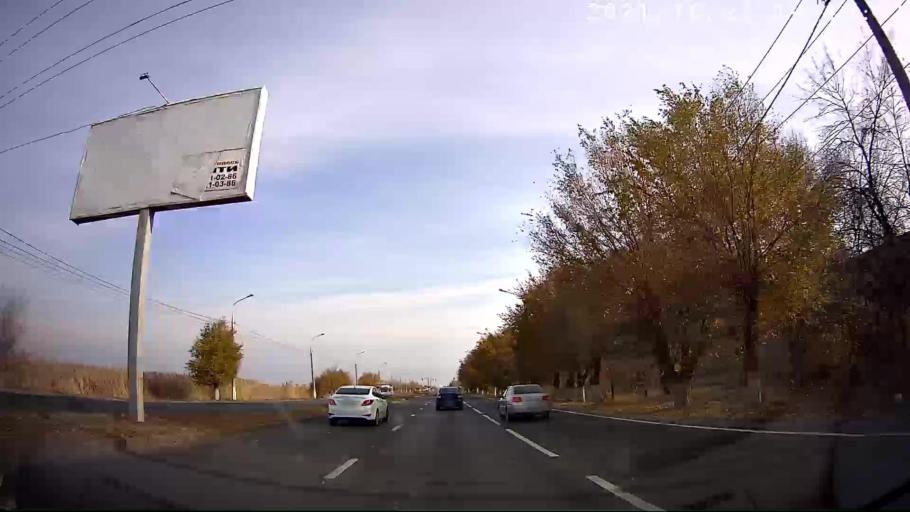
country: RU
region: Volgograd
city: Volgograd
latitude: 48.5308
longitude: 44.4763
